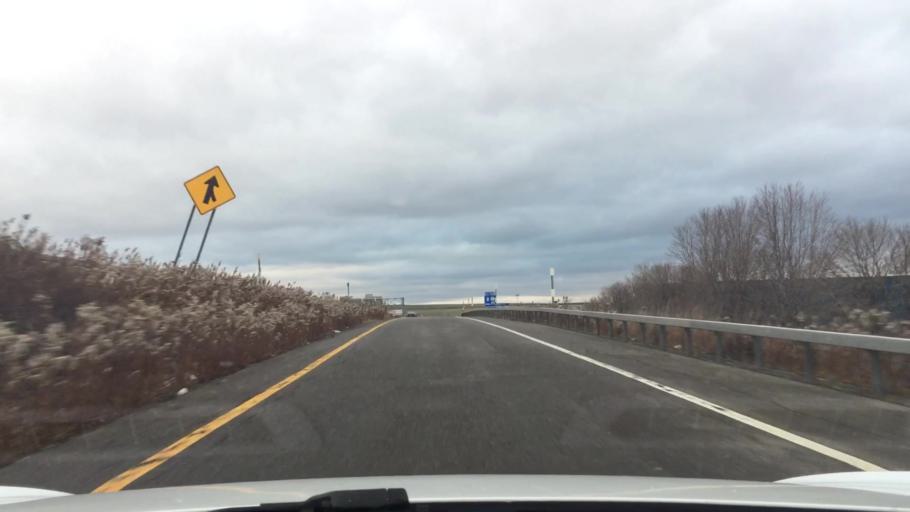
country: US
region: New York
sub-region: Niagara County
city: Niagara Falls
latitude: 43.0822
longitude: -78.9905
